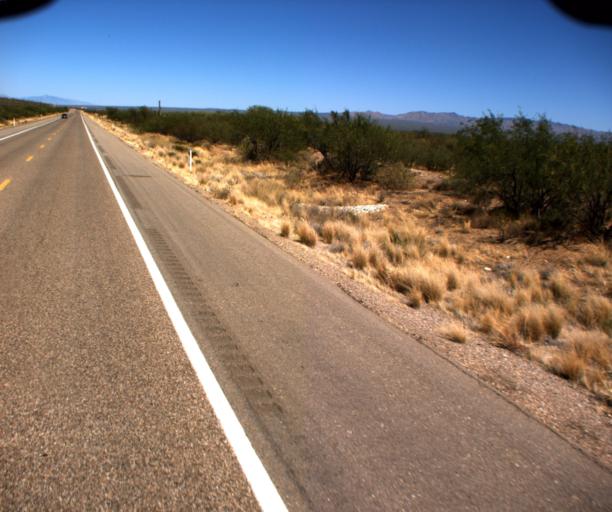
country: US
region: Arizona
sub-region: Pima County
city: Three Points
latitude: 32.0410
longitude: -111.4571
